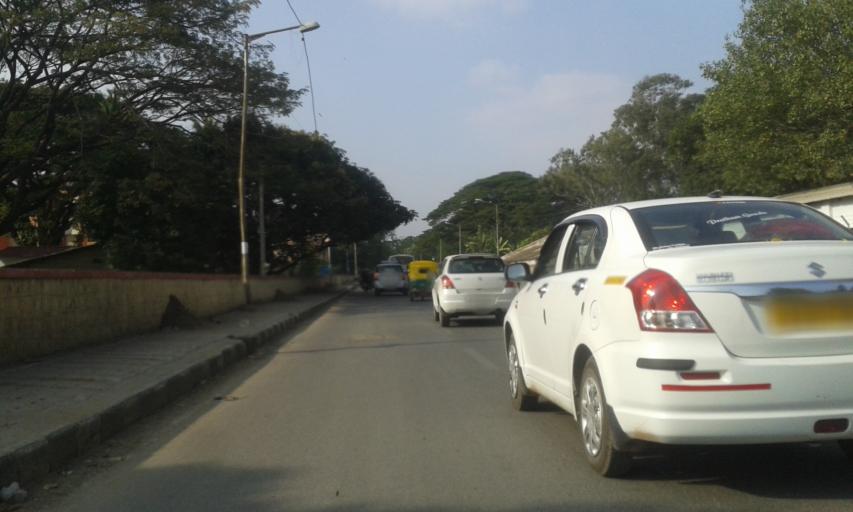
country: IN
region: Karnataka
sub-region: Bangalore Urban
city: Bangalore
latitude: 12.9606
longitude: 77.6196
